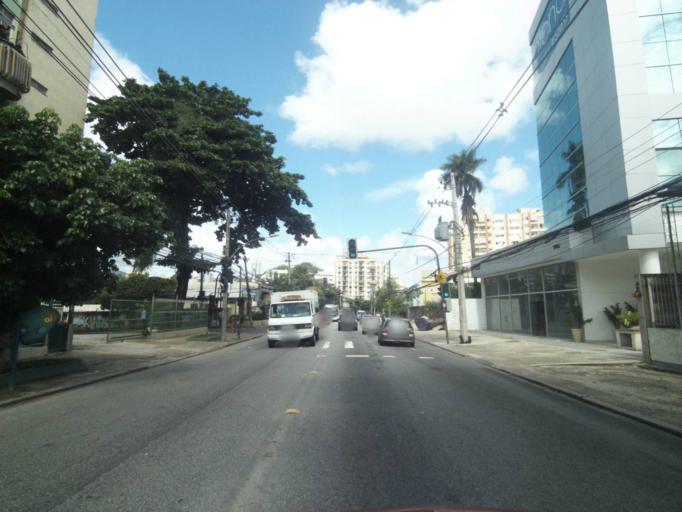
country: BR
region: Rio de Janeiro
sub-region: Sao Joao De Meriti
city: Sao Joao de Meriti
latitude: -22.9328
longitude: -43.3529
